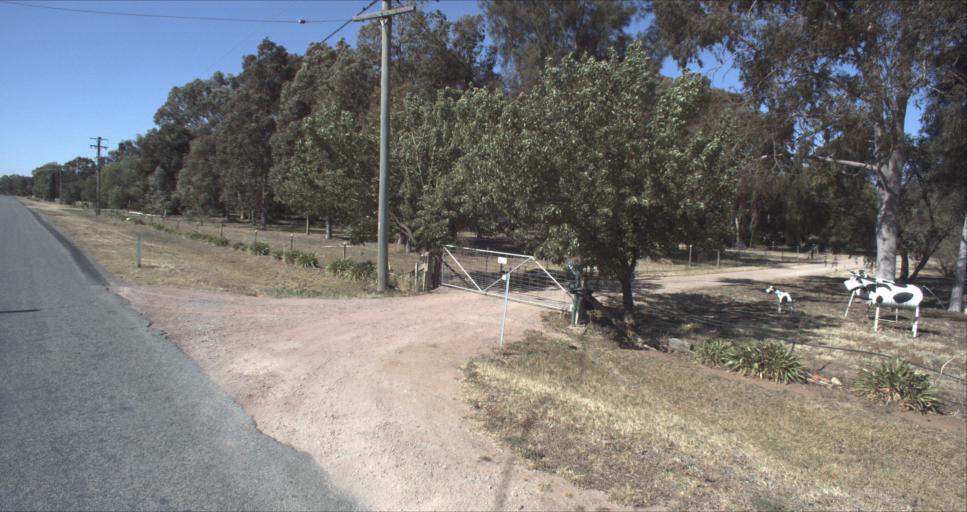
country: AU
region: New South Wales
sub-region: Leeton
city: Leeton
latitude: -34.5406
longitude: 146.4191
